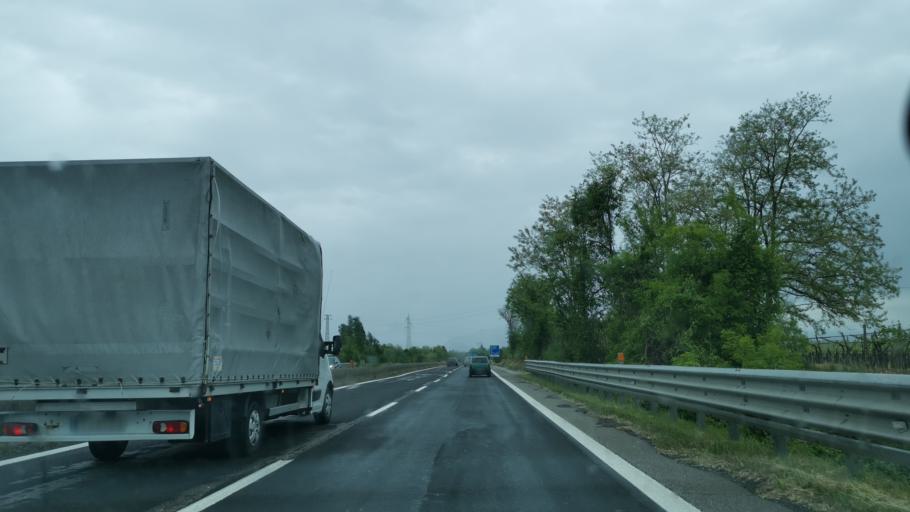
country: IT
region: Veneto
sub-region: Provincia di Verona
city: Cola
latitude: 45.4597
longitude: 10.7556
